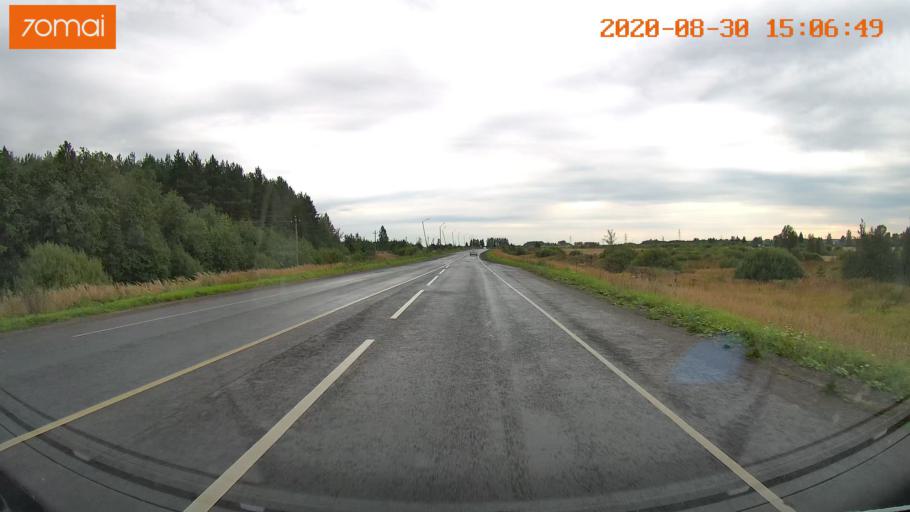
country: RU
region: Ivanovo
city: Staraya Vichuga
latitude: 57.2534
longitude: 41.9004
